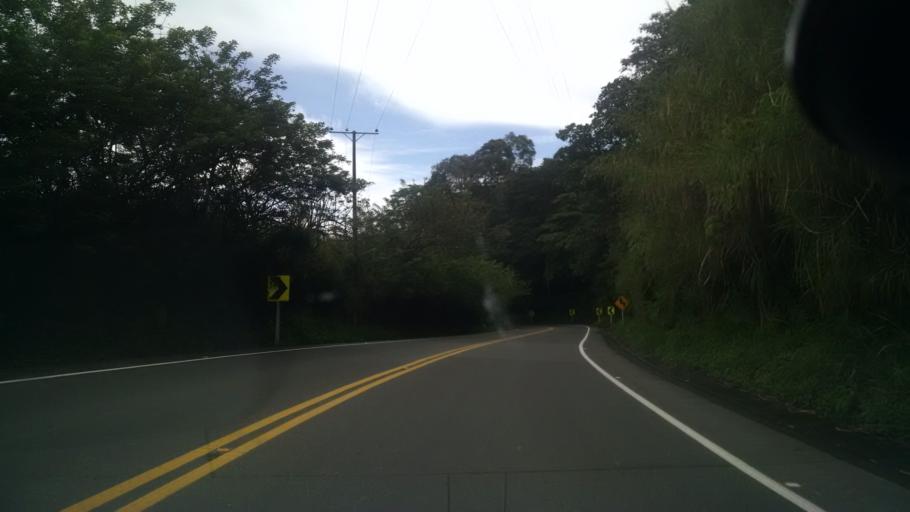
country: CO
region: Caldas
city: Palestina
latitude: 5.0526
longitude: -75.6045
